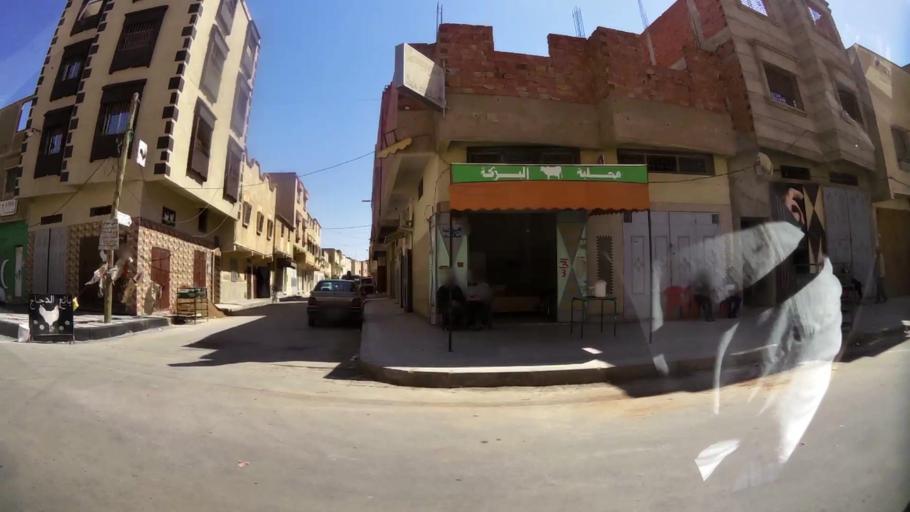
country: MA
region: Oriental
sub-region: Oujda-Angad
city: Oujda
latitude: 34.6864
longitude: -1.9370
